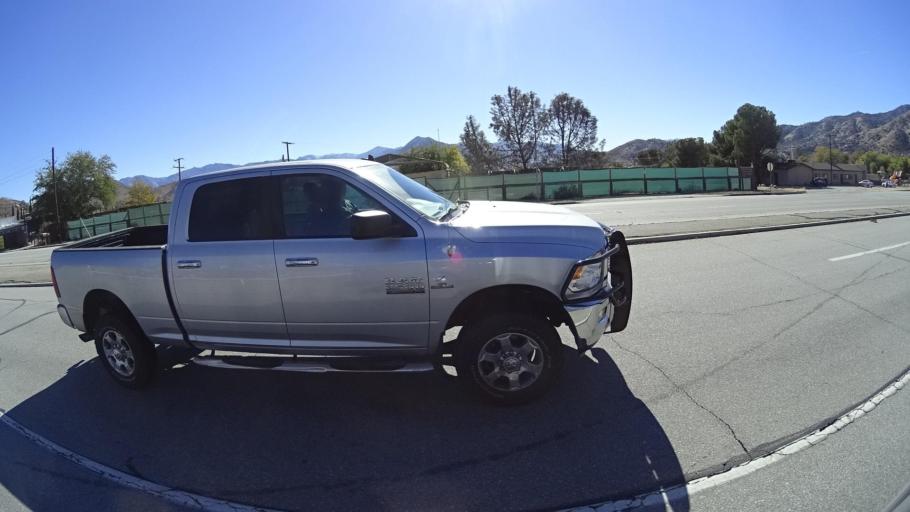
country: US
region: California
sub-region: Kern County
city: Wofford Heights
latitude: 35.7085
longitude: -118.4509
